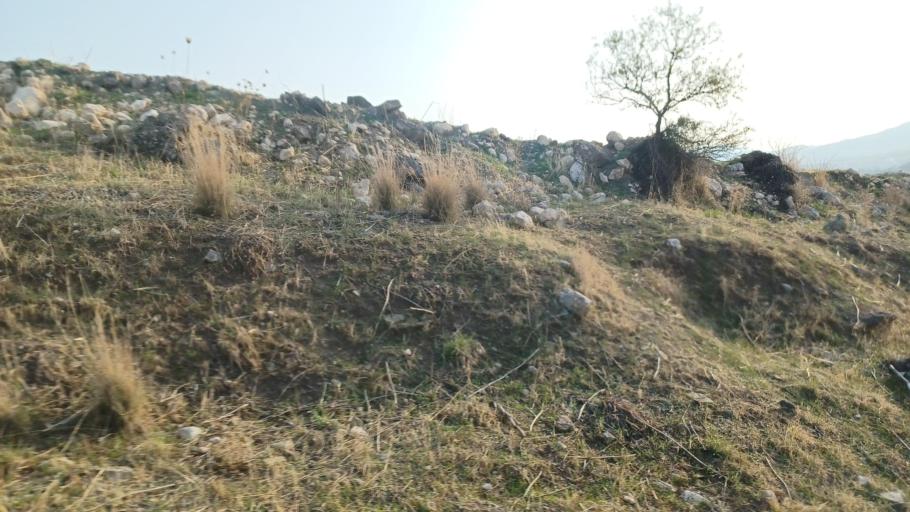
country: CY
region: Pafos
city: Polis
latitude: 34.9607
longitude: 32.4908
